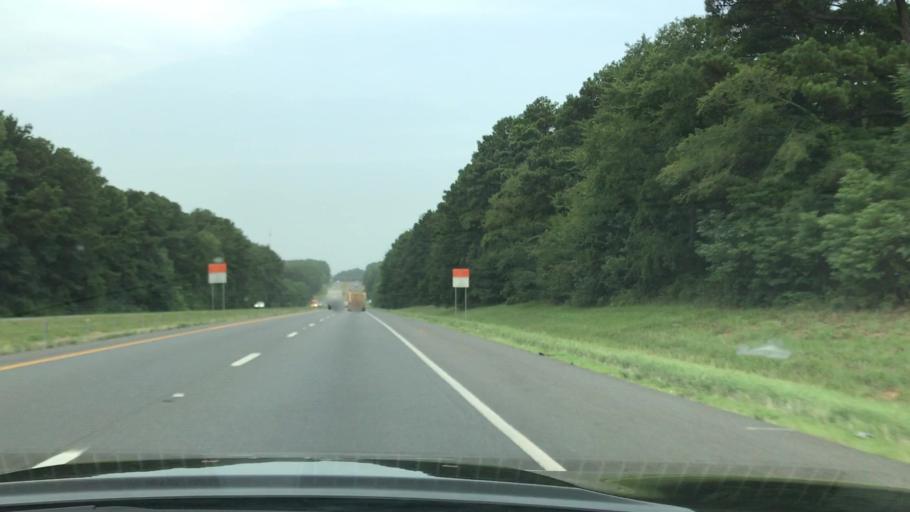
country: US
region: Texas
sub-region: Harrison County
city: Marshall
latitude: 32.4889
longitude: -94.4158
